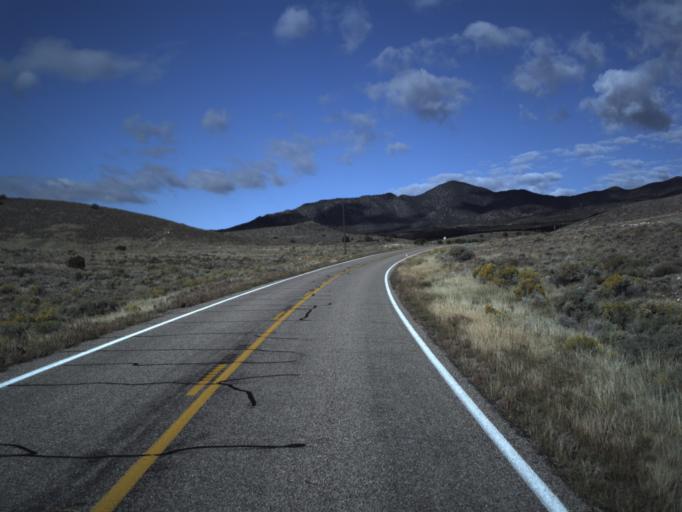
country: US
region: Utah
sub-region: Beaver County
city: Milford
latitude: 38.4570
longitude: -113.2238
